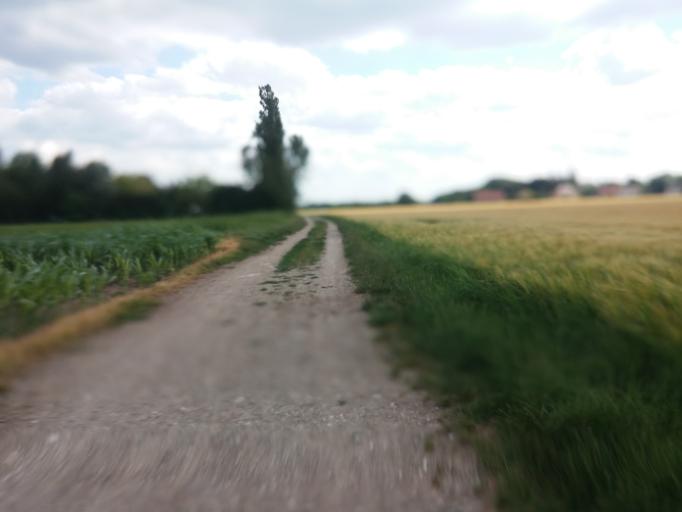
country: DE
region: Bavaria
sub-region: Upper Bavaria
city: Unterfoehring
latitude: 48.1559
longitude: 11.6633
